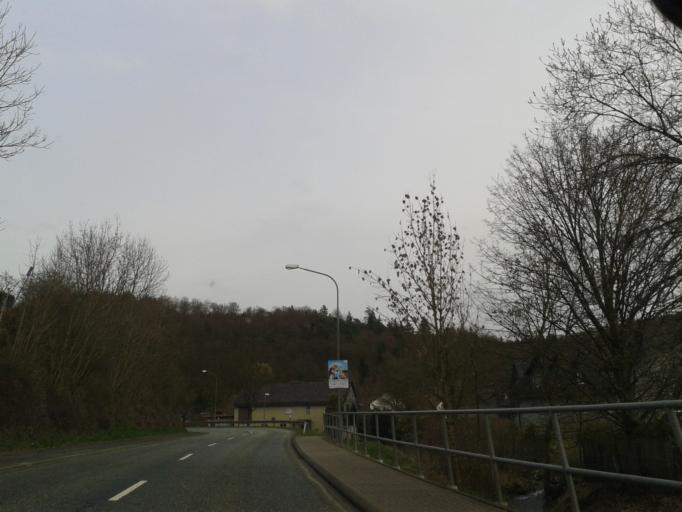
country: DE
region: Hesse
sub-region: Regierungsbezirk Giessen
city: Siegbach
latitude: 50.8093
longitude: 8.4368
